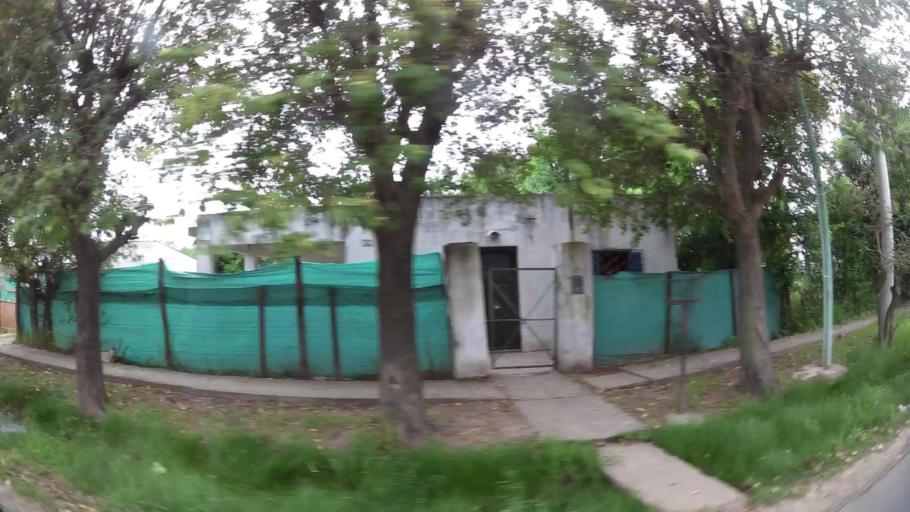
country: AR
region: Buenos Aires
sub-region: Partido de Campana
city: Campana
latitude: -34.2098
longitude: -58.9367
